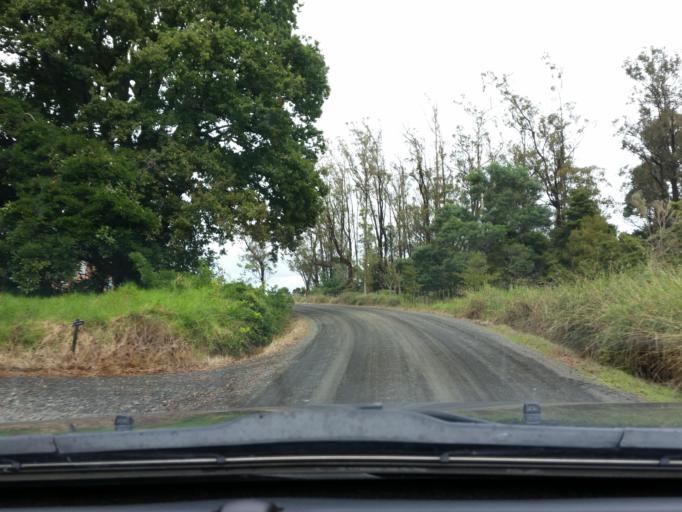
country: NZ
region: Northland
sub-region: Kaipara District
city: Dargaville
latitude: -35.8724
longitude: 174.0108
